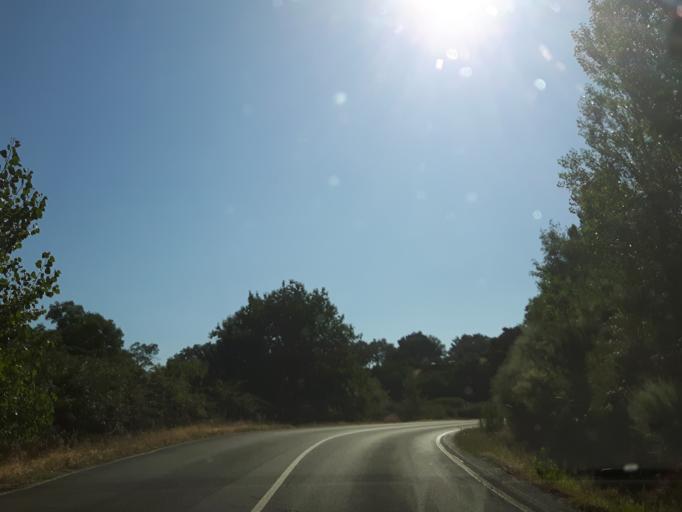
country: ES
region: Castille and Leon
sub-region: Provincia de Salamanca
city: Navalmoral de Bejar
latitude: 40.4079
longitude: -5.8069
